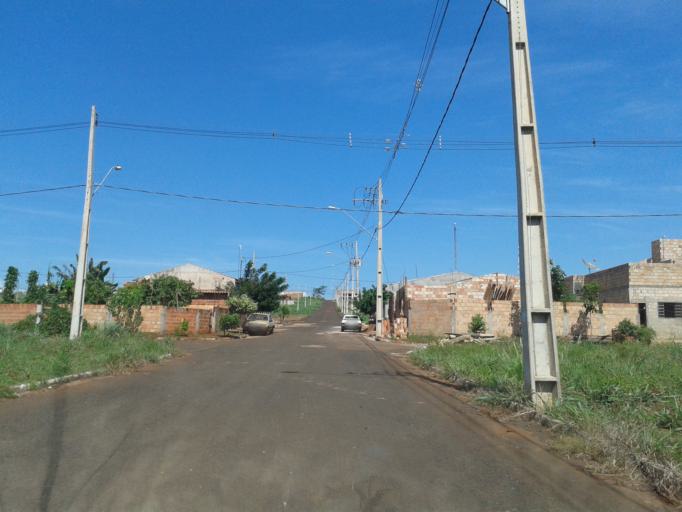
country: BR
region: Goias
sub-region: Itumbiara
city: Itumbiara
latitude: -18.4222
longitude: -49.1836
